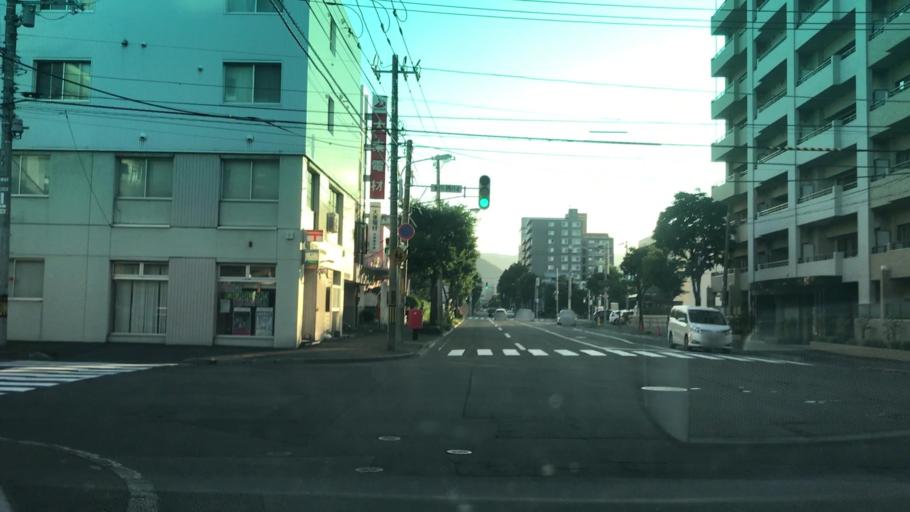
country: JP
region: Hokkaido
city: Sapporo
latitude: 43.0658
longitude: 141.3348
